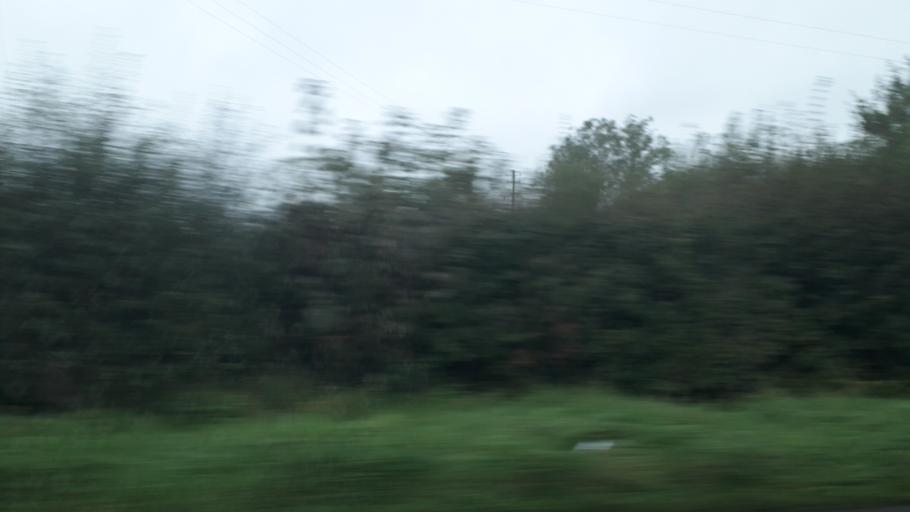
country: IE
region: Leinster
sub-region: An Longfort
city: Granard
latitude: 53.6328
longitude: -7.4789
